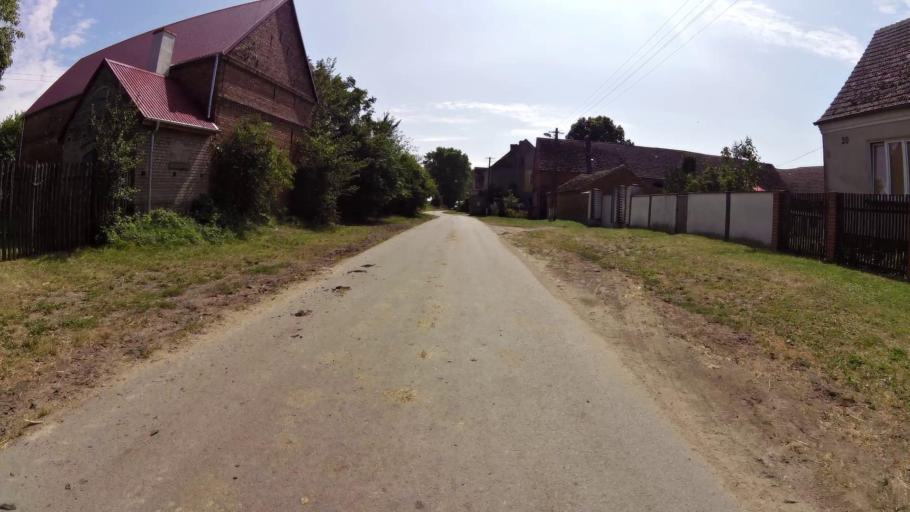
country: PL
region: West Pomeranian Voivodeship
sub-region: Powiat stargardzki
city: Suchan
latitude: 53.2664
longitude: 15.4060
